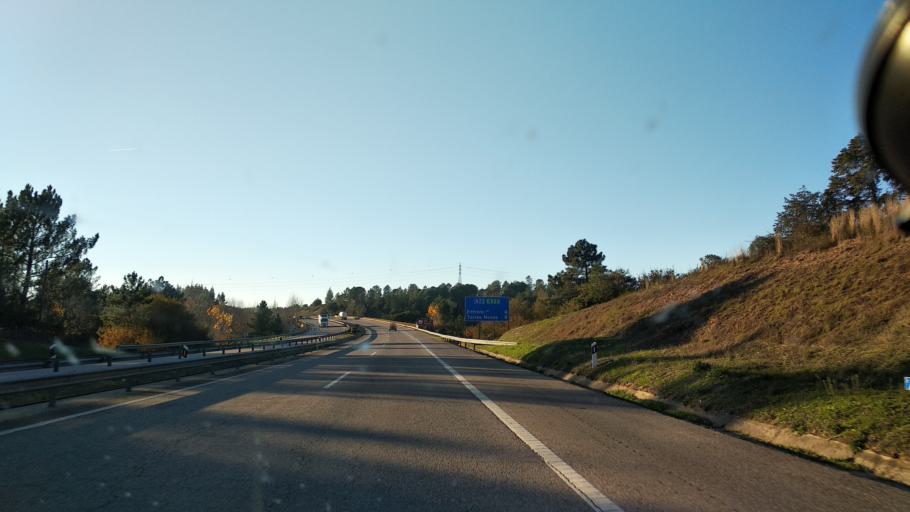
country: PT
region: Santarem
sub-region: Entroncamento
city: Entroncamento
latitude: 39.4895
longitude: -8.4533
